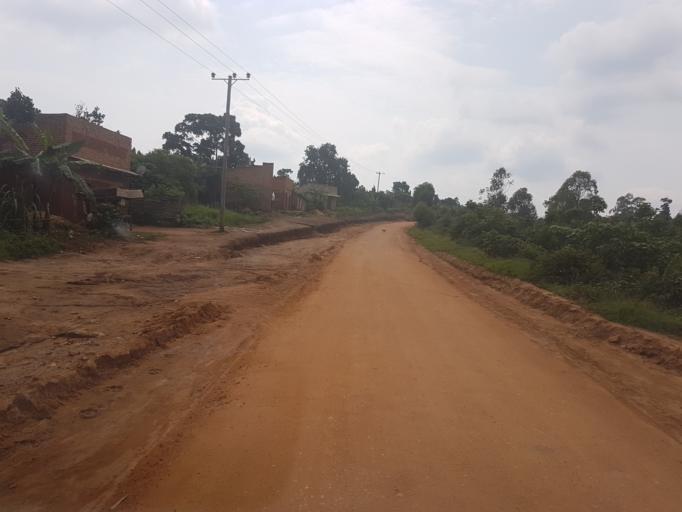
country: UG
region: Western Region
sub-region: Kanungu District
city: Ntungamo
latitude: -0.8179
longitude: 29.7069
